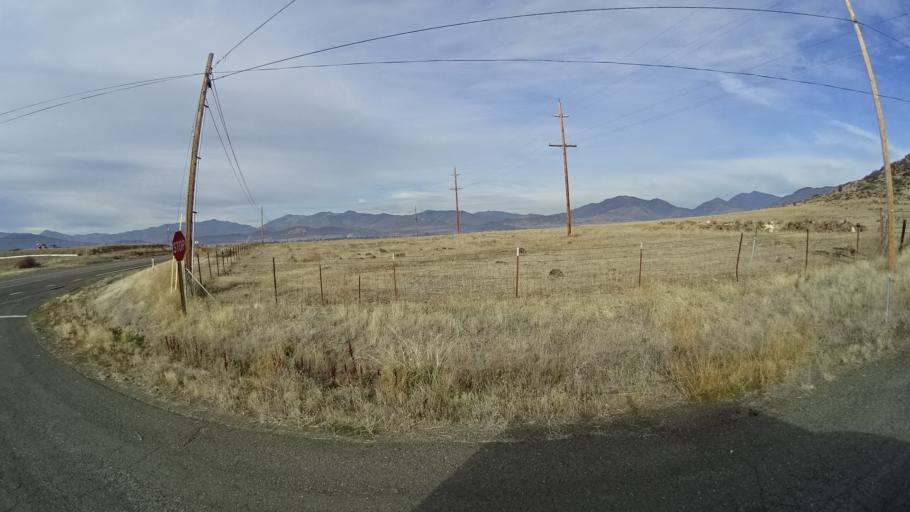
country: US
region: California
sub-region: Siskiyou County
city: Montague
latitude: 41.7248
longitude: -122.5464
